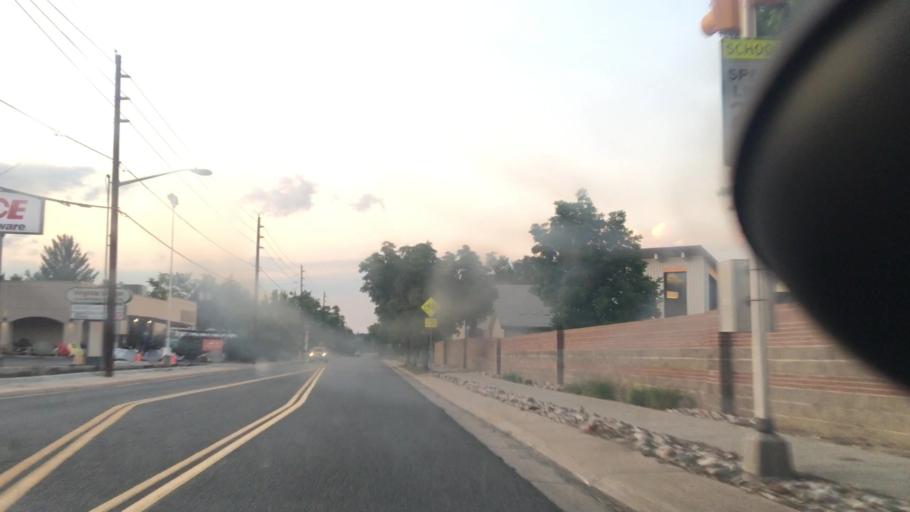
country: US
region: Colorado
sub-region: Arapahoe County
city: Glendale
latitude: 39.6898
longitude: -104.9223
